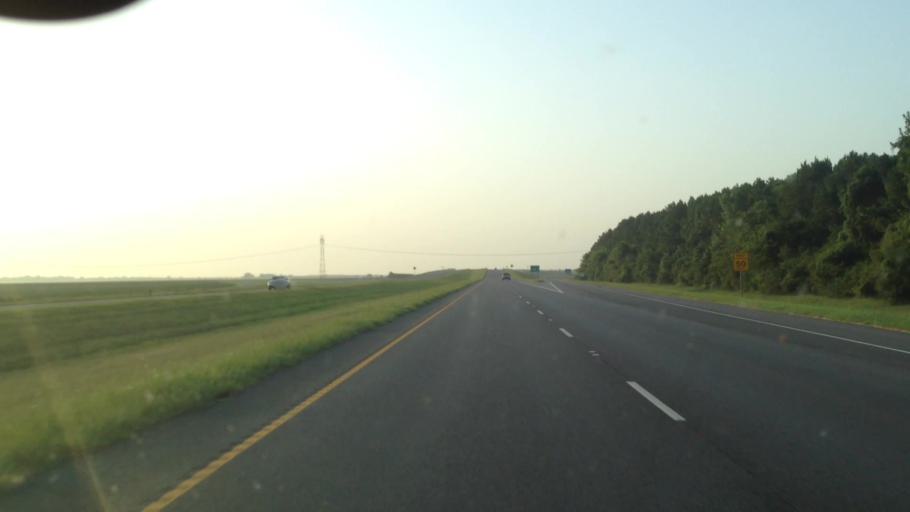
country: US
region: Louisiana
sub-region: Natchitoches Parish
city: Campti
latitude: 31.8417
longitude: -93.2845
